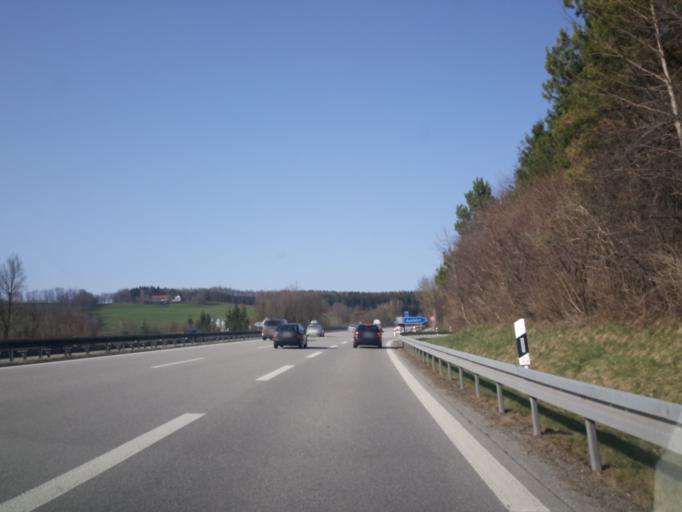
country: DE
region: Bavaria
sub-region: Upper Bavaria
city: Sindelsdorf
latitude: 47.7261
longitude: 11.3247
